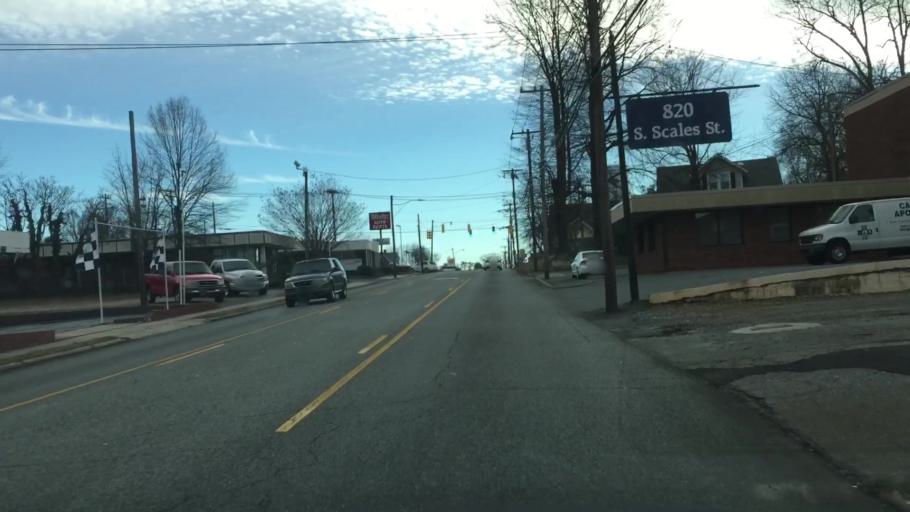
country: US
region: North Carolina
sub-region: Rockingham County
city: Reidsville
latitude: 36.3499
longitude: -79.6650
